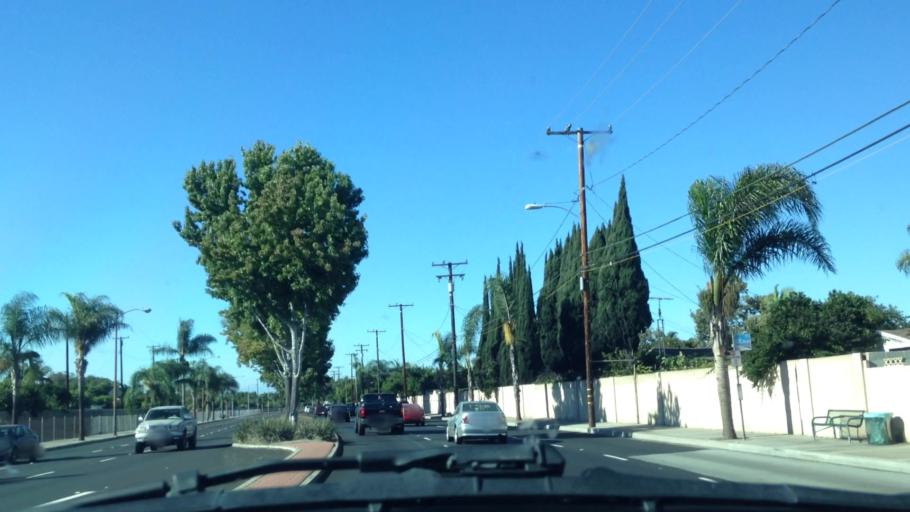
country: US
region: California
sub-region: Orange County
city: Santa Ana
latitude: 33.7293
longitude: -117.9058
